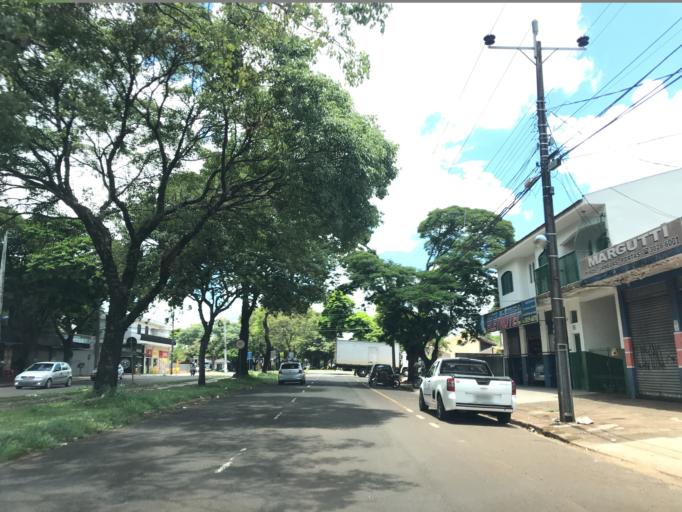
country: BR
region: Parana
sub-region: Maringa
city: Maringa
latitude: -23.3944
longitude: -51.9178
